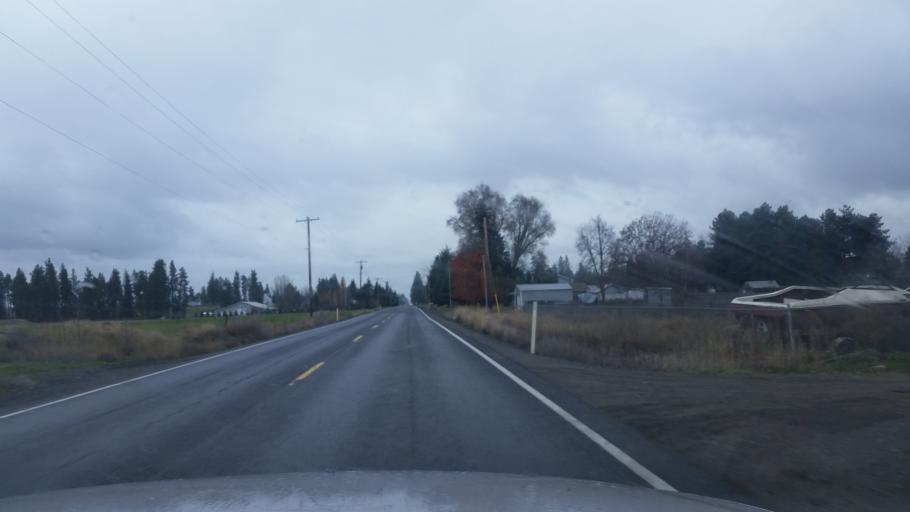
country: US
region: Washington
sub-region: Spokane County
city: Spokane
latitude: 47.6136
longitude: -117.4969
